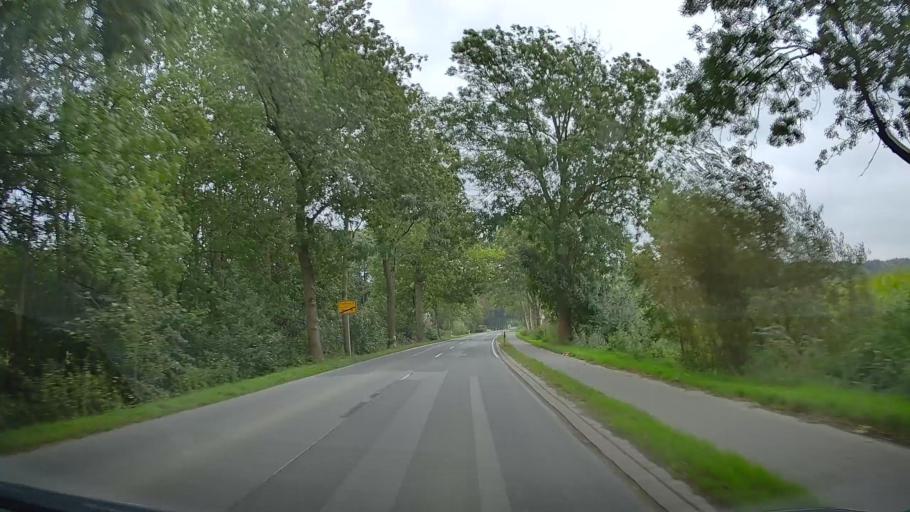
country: DE
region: Lower Saxony
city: Geversdorf
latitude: 53.8207
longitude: 9.0949
